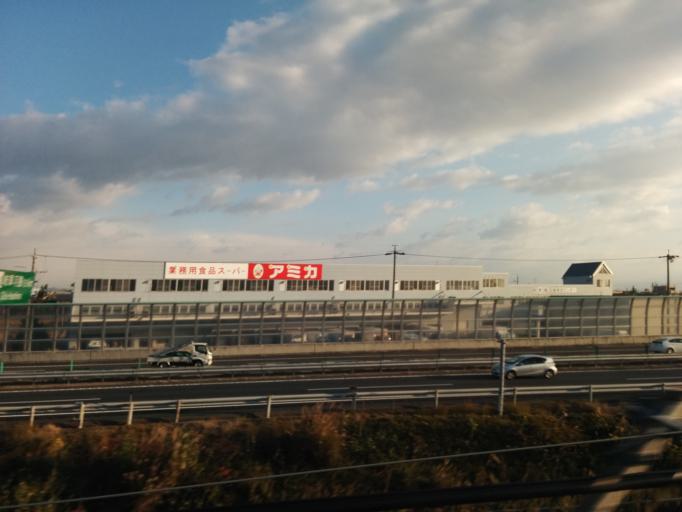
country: JP
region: Aichi
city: Sobue
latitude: 35.3023
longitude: 136.7081
